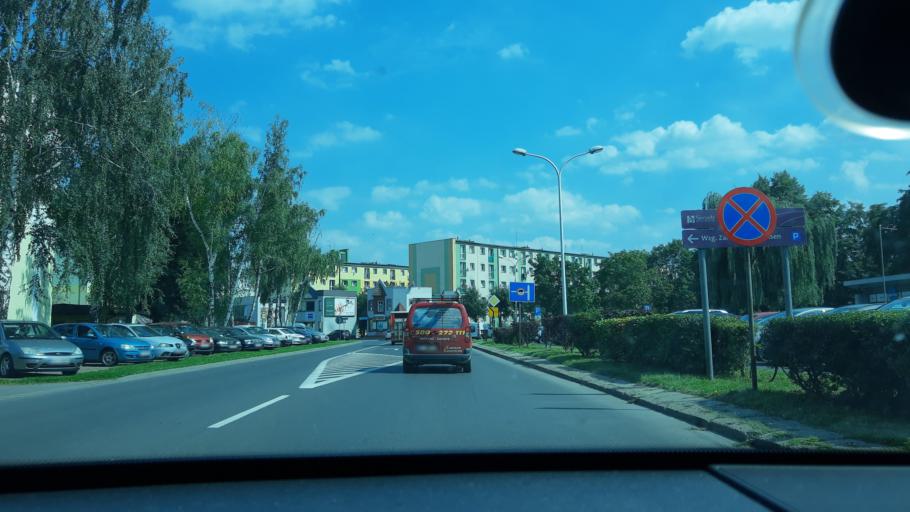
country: PL
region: Lodz Voivodeship
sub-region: Powiat sieradzki
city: Sieradz
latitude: 51.5898
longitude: 18.7296
